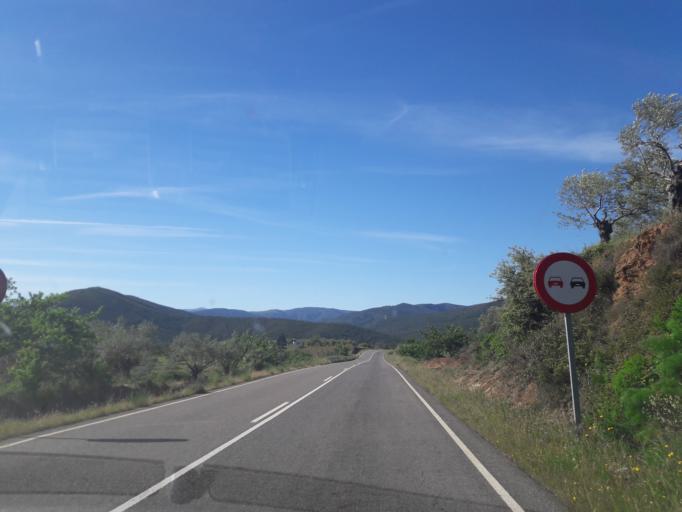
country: ES
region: Castille and Leon
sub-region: Provincia de Salamanca
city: Sotoserrano
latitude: 40.4278
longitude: -6.0330
